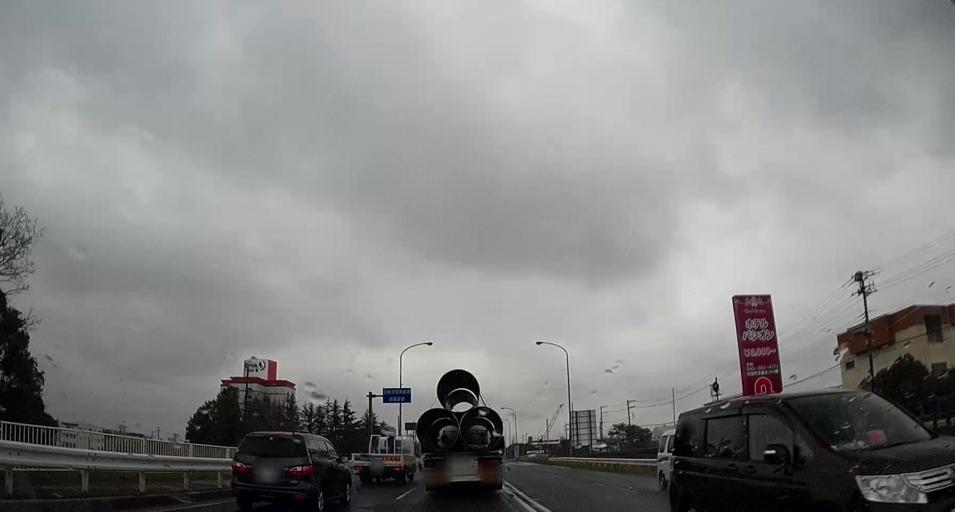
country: JP
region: Chiba
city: Ichihara
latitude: 35.5416
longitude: 140.1167
